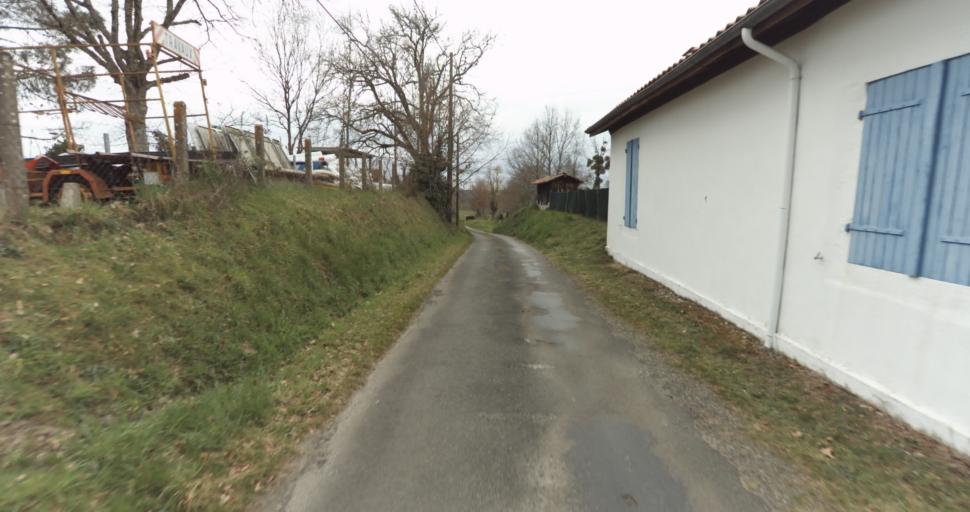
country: FR
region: Aquitaine
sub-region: Departement des Landes
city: Roquefort
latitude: 44.0301
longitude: -0.3249
